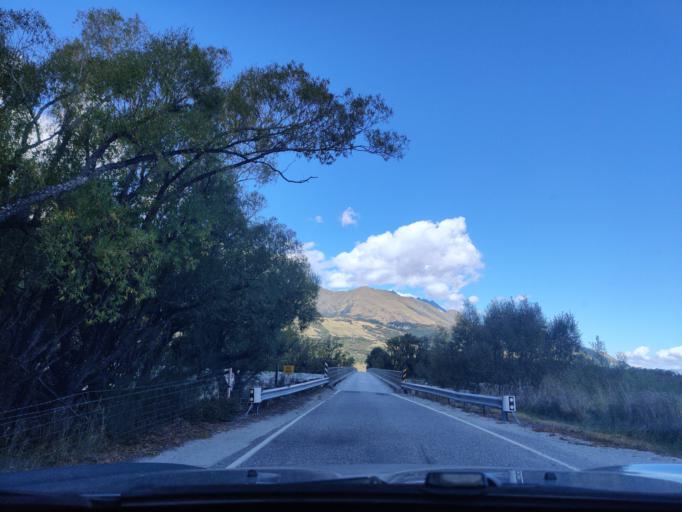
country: NZ
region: Otago
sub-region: Queenstown-Lakes District
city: Queenstown
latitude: -44.7861
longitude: 168.3957
